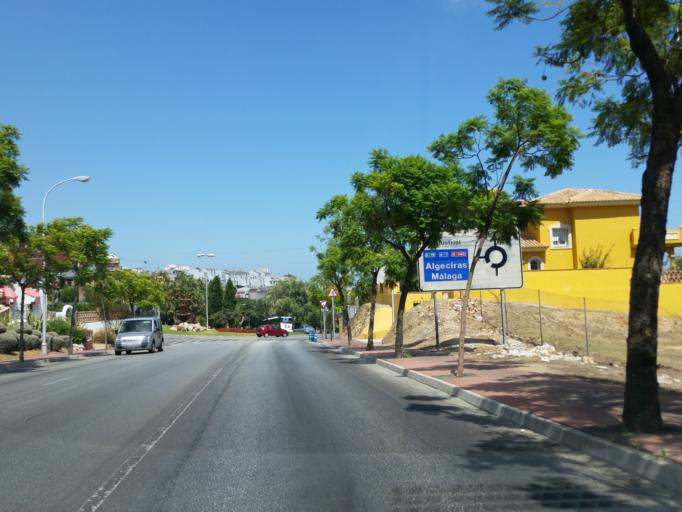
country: ES
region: Andalusia
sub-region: Provincia de Malaga
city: Benalmadena
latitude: 36.6013
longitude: -4.5511
